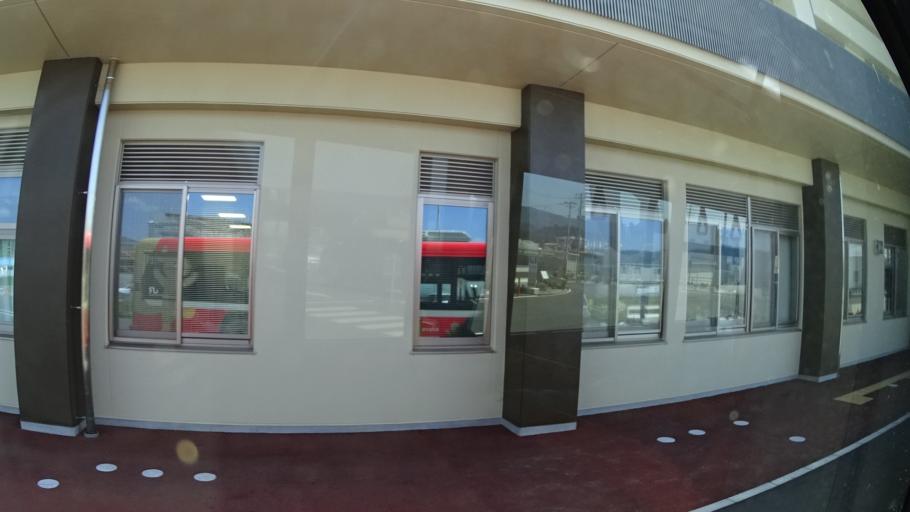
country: JP
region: Iwate
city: Ofunato
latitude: 39.0257
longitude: 141.6416
